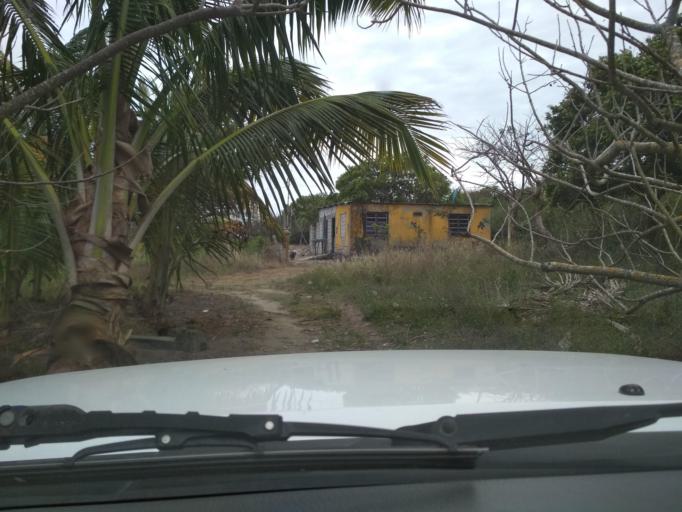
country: MX
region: Veracruz
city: Anton Lizardo
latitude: 19.0494
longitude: -95.9905
